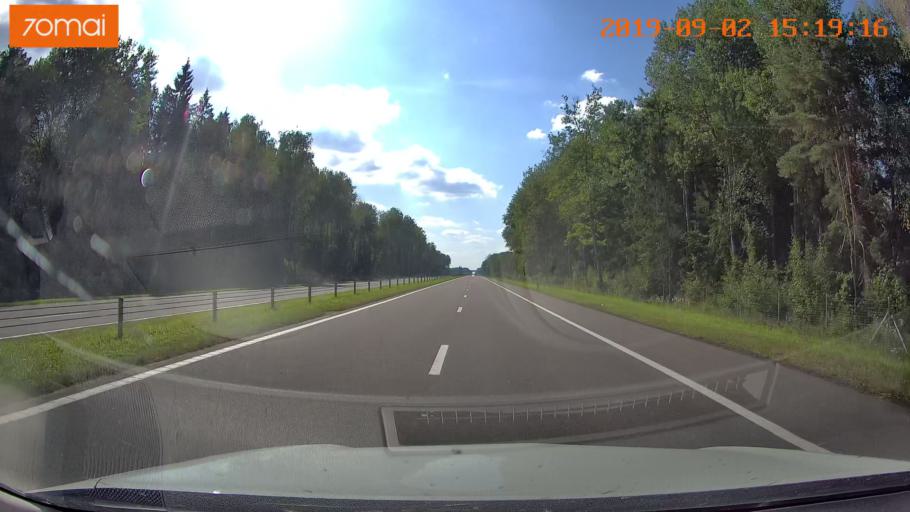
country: BY
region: Mogilev
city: Byalynichy
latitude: 53.9351
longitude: 29.5404
